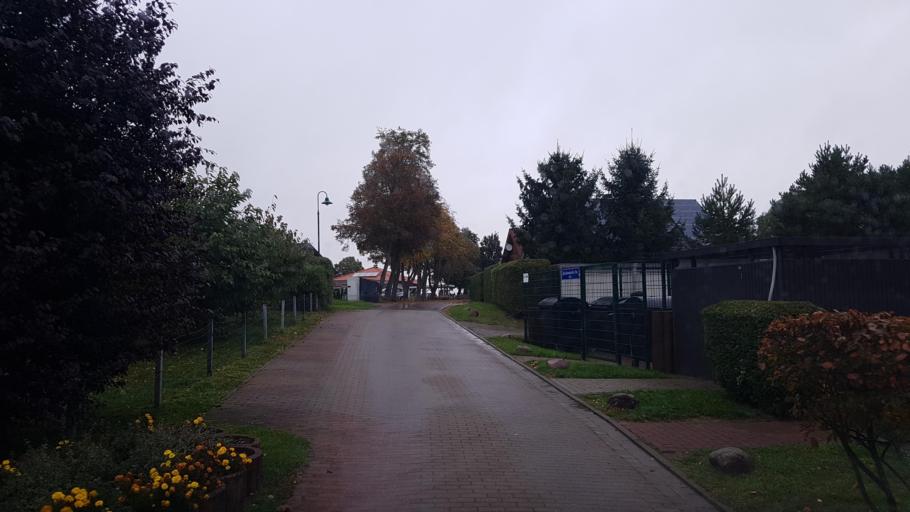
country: DE
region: Brandenburg
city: Furstenwalde
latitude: 52.4296
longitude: 14.0354
